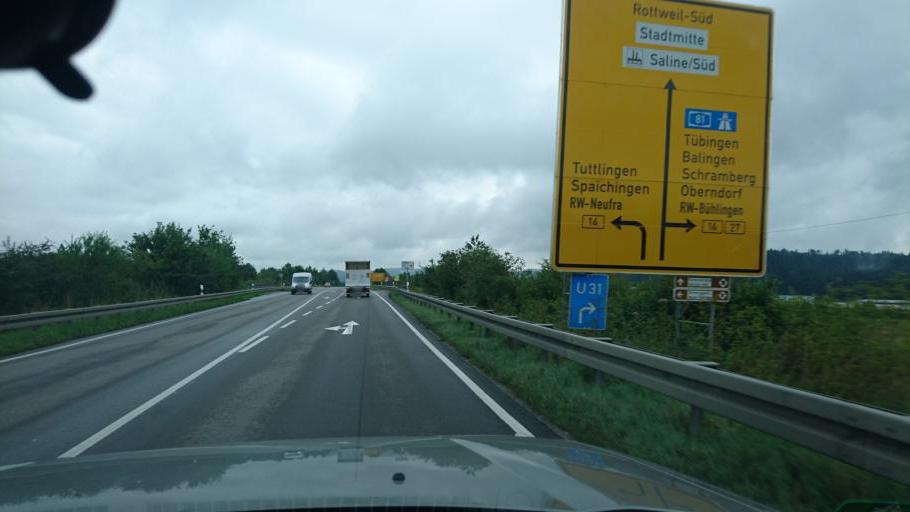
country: DE
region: Baden-Wuerttemberg
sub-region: Freiburg Region
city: Rottweil
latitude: 48.1406
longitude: 8.6372
